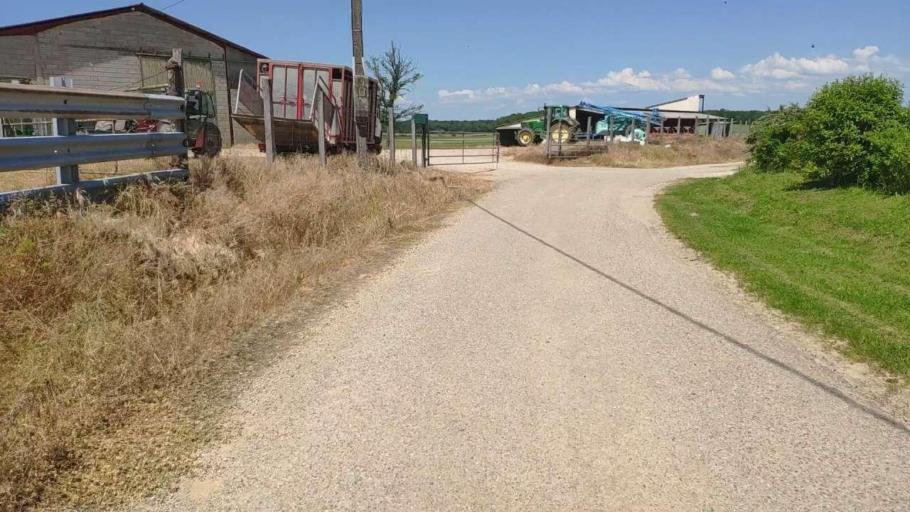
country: FR
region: Franche-Comte
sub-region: Departement du Jura
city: Bletterans
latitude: 46.7442
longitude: 5.3717
